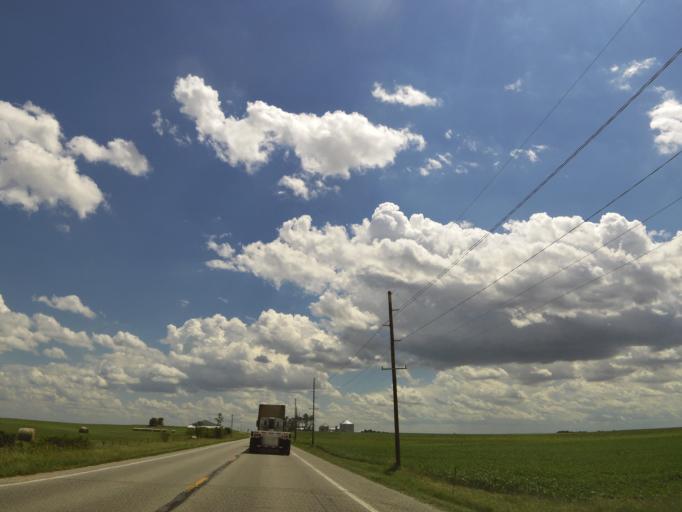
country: US
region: Iowa
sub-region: Benton County
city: Urbana
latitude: 42.2905
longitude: -91.8898
